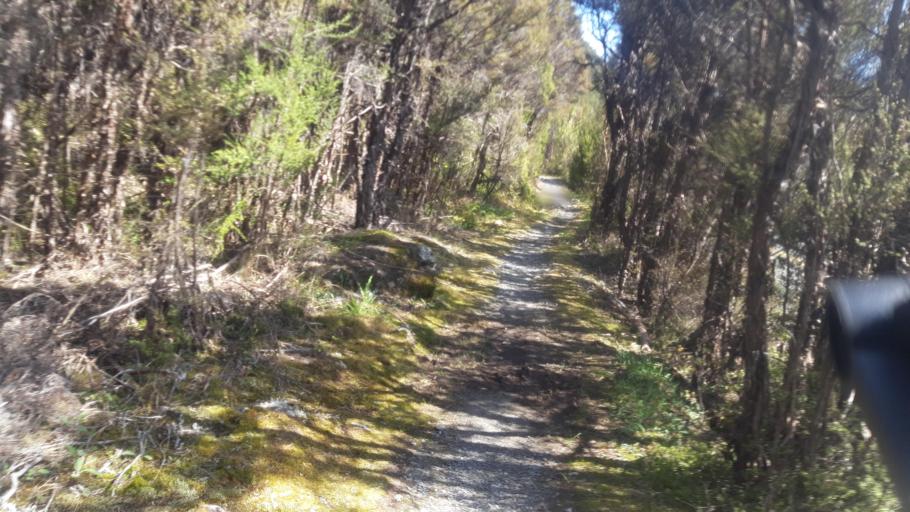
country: NZ
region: Tasman
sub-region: Tasman District
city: Wakefield
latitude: -41.8010
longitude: 172.8397
